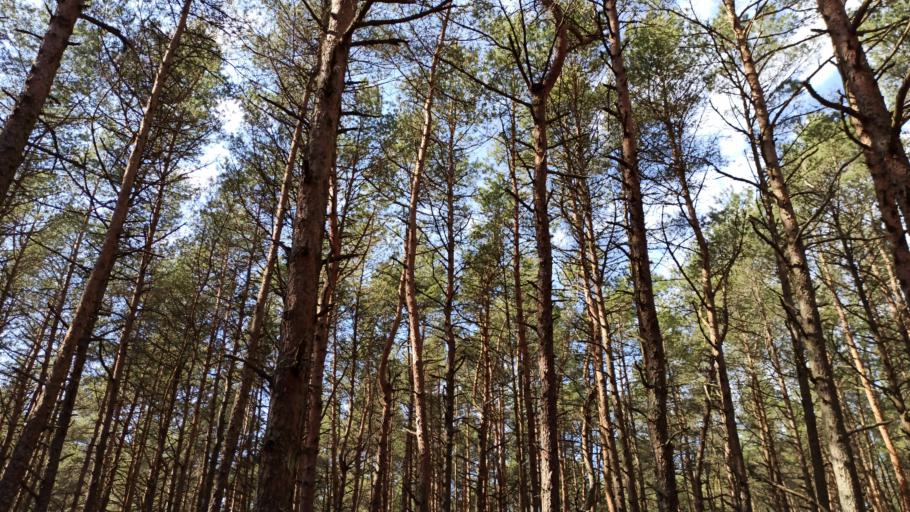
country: LT
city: Nida
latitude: 55.1798
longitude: 20.8633
